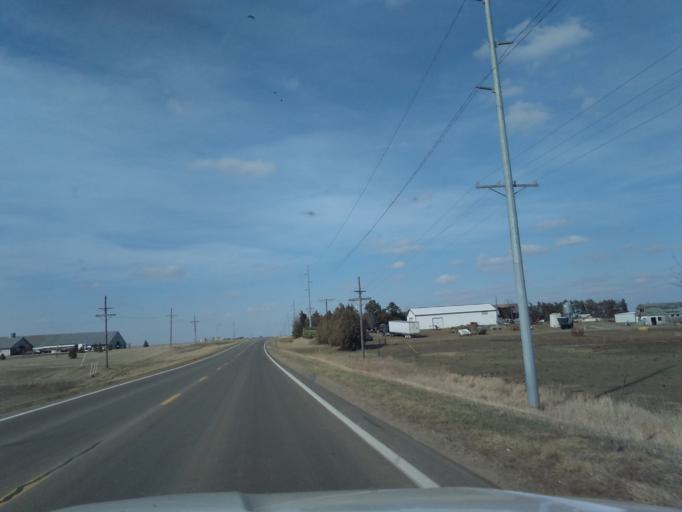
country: US
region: Nebraska
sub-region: Gage County
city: Beatrice
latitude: 40.1858
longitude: -96.9353
